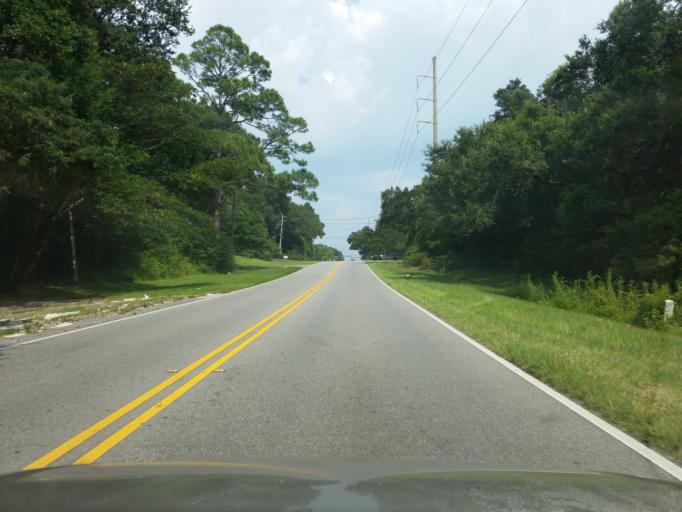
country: US
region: Florida
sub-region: Escambia County
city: Ferry Pass
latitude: 30.5309
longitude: -87.2128
